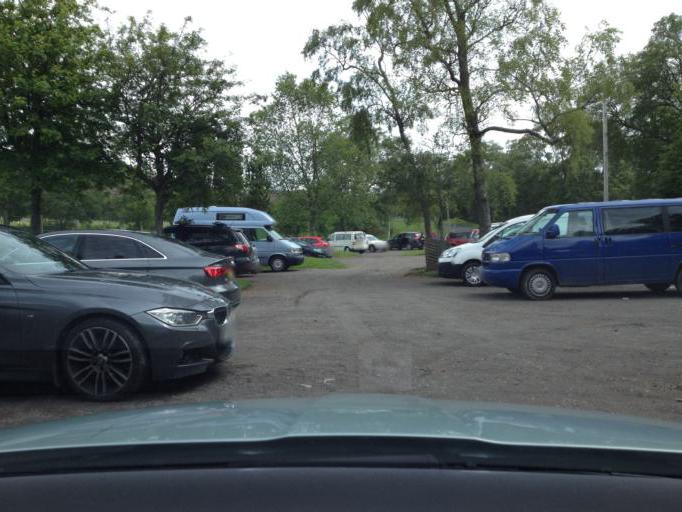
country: GB
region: Scotland
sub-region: Aberdeenshire
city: Ballater
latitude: 56.9114
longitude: -2.9105
